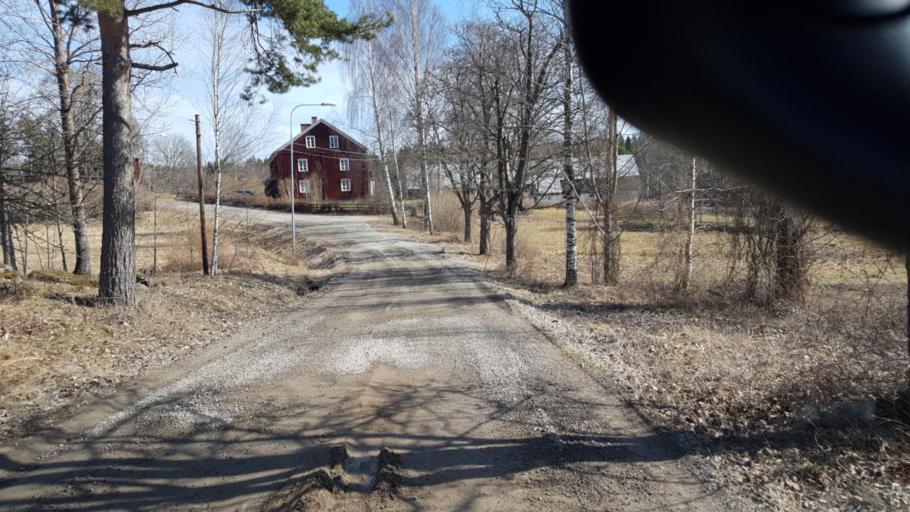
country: SE
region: Vaermland
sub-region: Arvika Kommun
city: Arvika
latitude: 59.5291
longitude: 12.8366
